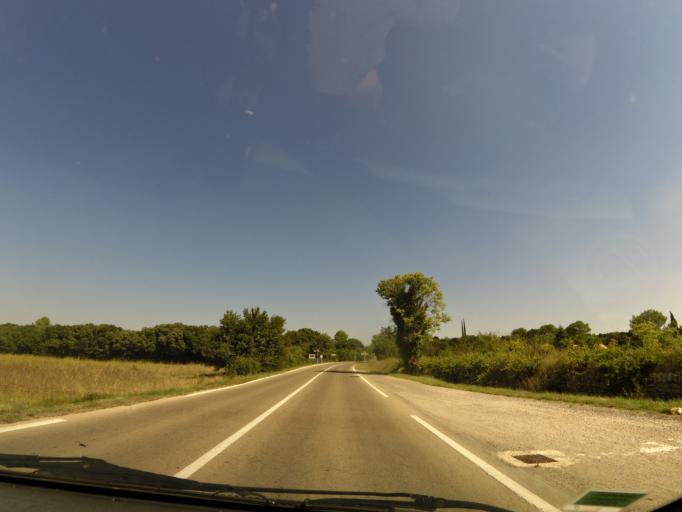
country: FR
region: Languedoc-Roussillon
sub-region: Departement du Gard
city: Villevieille
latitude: 43.8002
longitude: 4.1056
